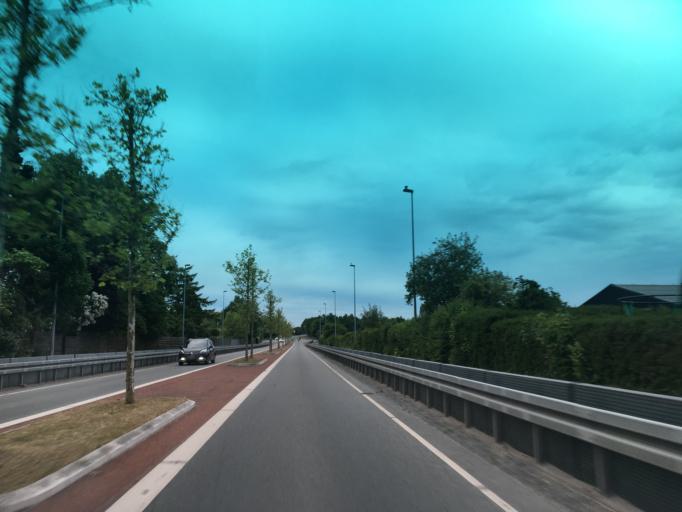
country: DK
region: Capital Region
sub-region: Albertslund Kommune
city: Albertslund
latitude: 55.6461
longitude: 12.3554
